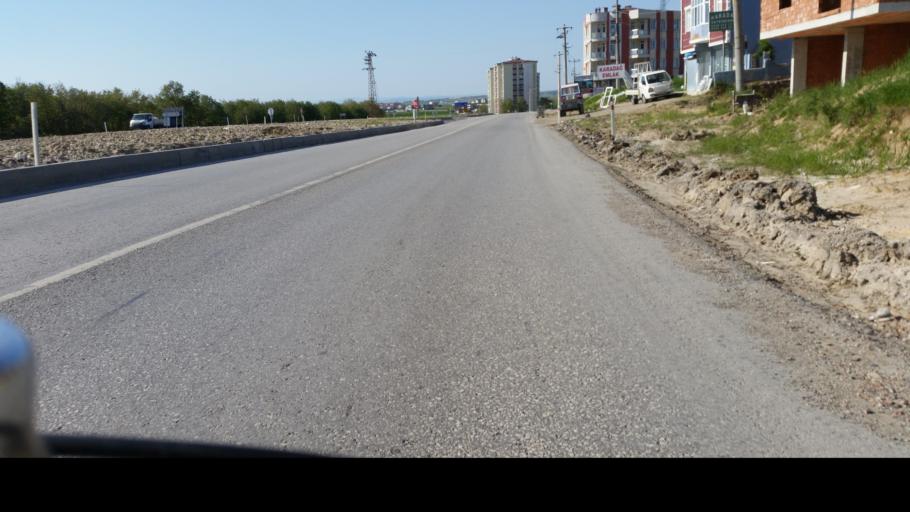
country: TR
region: Tekirdag
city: Saray
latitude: 41.3629
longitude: 27.9424
